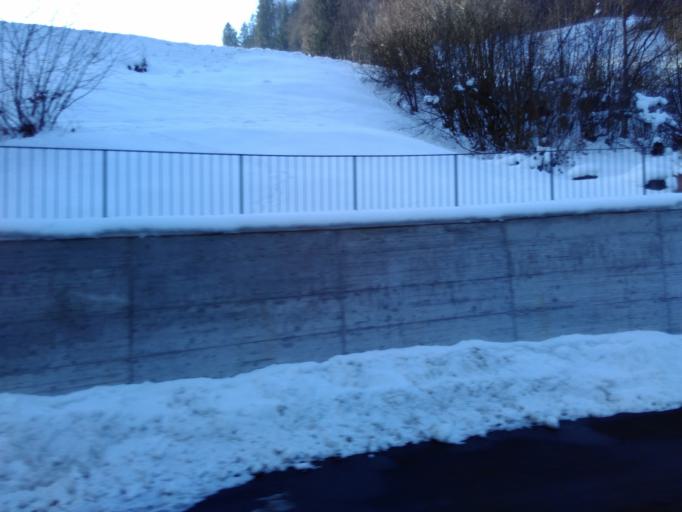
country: CH
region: Schwyz
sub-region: Bezirk March
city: Vorderthal
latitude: 47.1447
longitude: 8.8963
